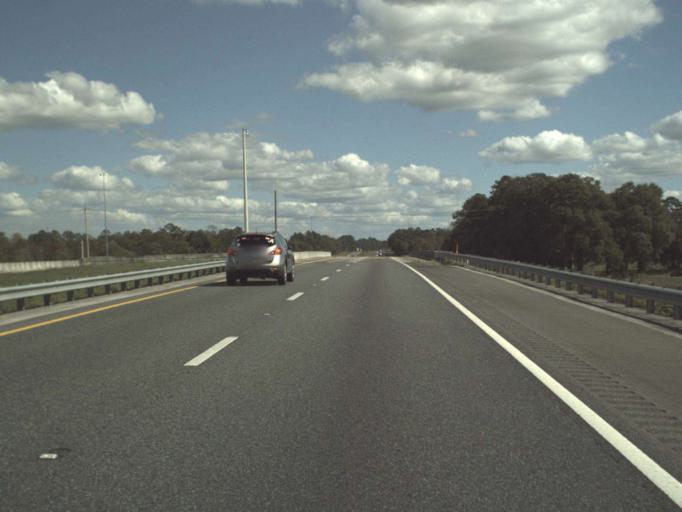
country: US
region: Florida
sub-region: Jackson County
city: Marianna
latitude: 30.7215
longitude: -85.1867
